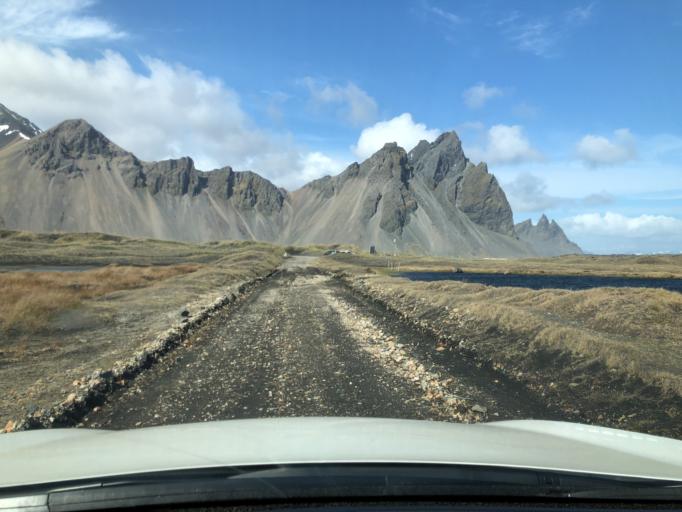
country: IS
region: East
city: Hoefn
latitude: 64.2429
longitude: -14.9716
